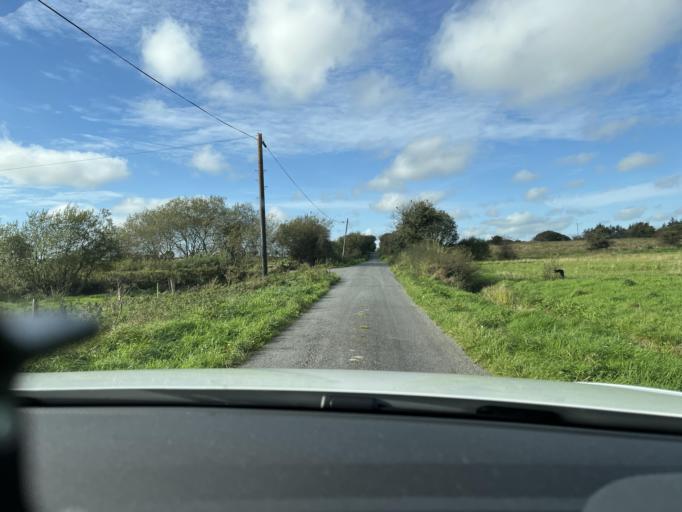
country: IE
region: Connaught
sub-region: Sligo
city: Ballymote
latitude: 54.0736
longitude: -8.4335
